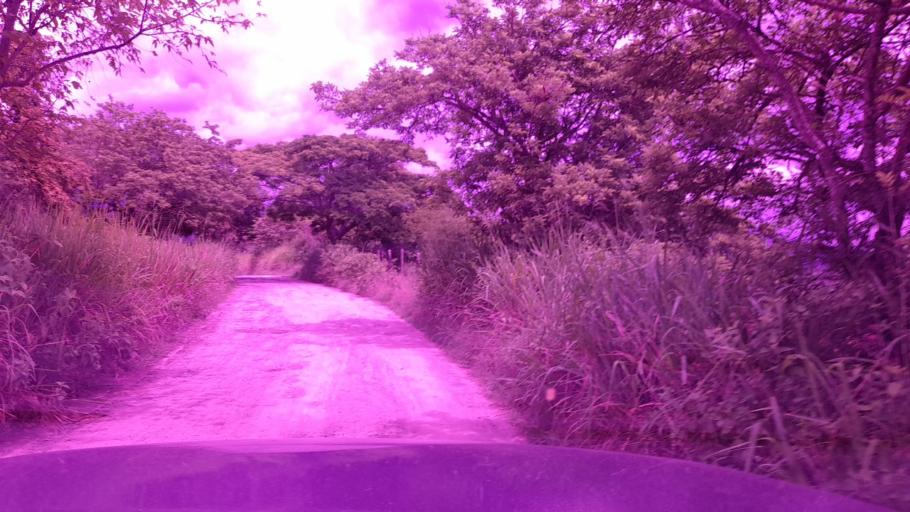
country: CO
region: Valle del Cauca
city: Bugalagrande
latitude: 4.1935
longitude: -76.1428
